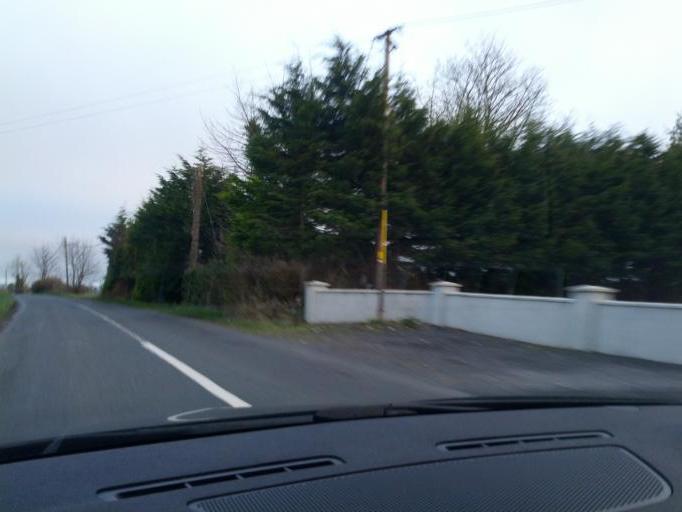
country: IE
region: Connaught
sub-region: Sligo
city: Ballymote
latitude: 54.0203
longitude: -8.5631
